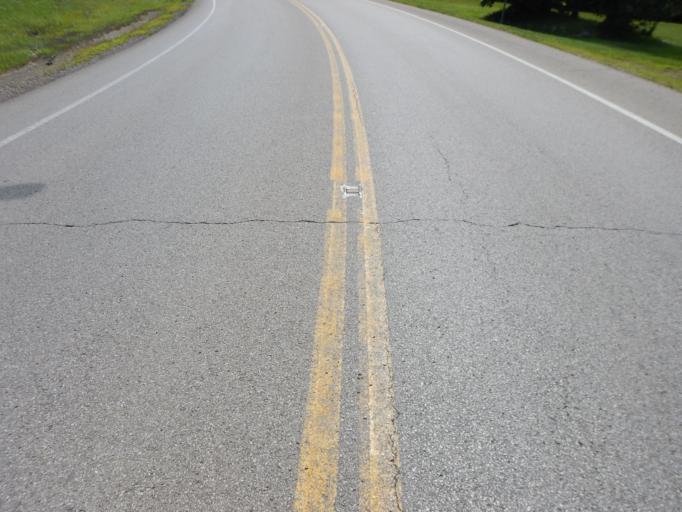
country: US
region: Ohio
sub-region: Muskingum County
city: Zanesville
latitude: 39.9544
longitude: -82.0216
